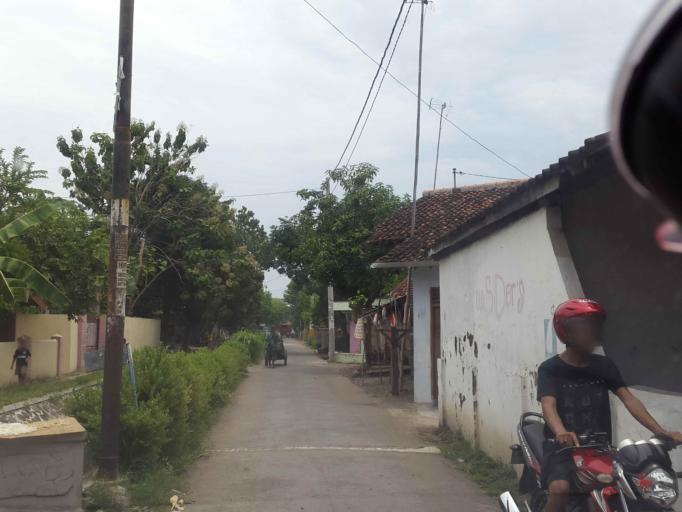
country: ID
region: Central Java
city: Tegal
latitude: -6.8759
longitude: 109.1137
